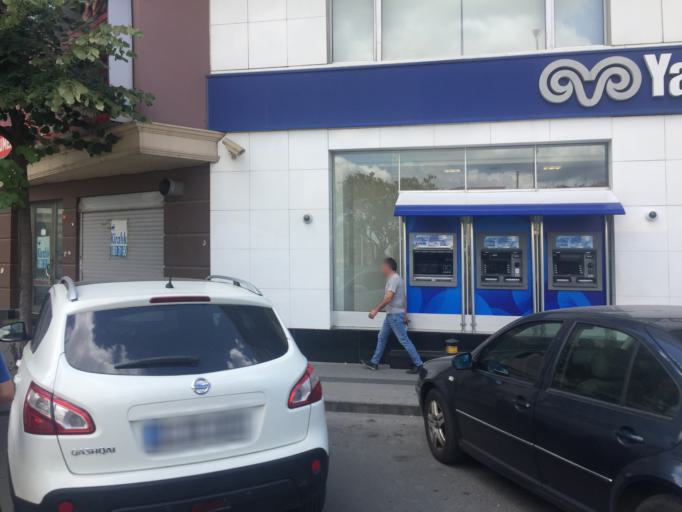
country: TR
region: Istanbul
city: merter keresteciler
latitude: 41.0339
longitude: 28.9120
